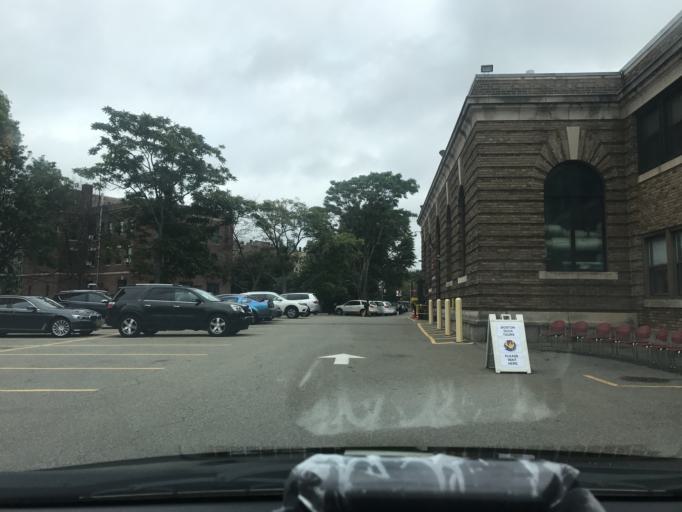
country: US
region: Massachusetts
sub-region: Norfolk County
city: Brookline
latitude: 42.3364
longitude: -71.0961
